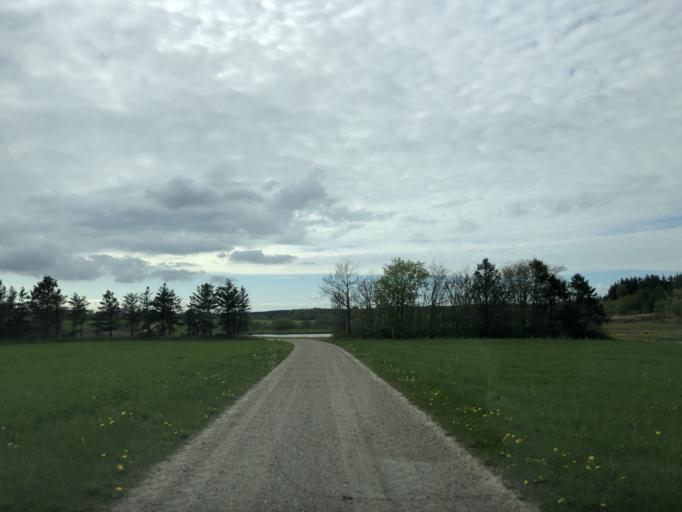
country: DK
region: Central Jutland
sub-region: Holstebro Kommune
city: Ulfborg
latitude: 56.1941
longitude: 8.4657
